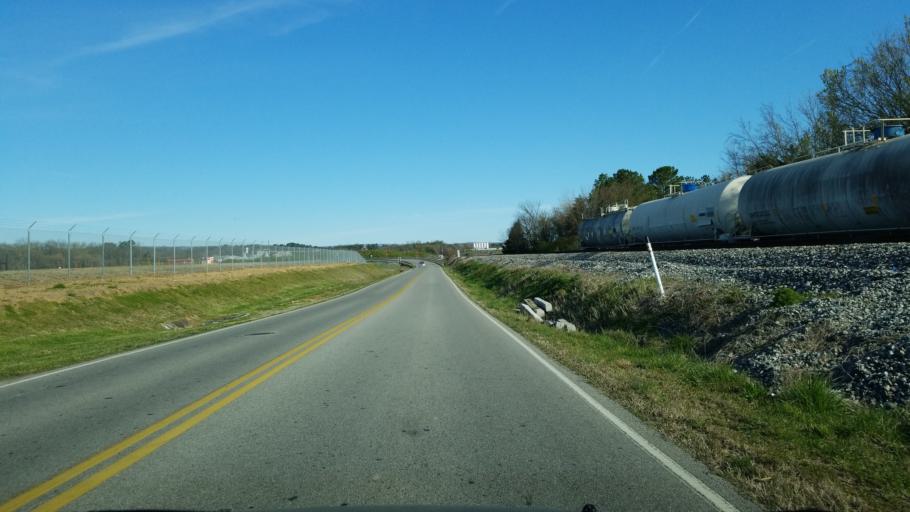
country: US
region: Tennessee
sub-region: Hamilton County
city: East Chattanooga
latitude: 35.0425
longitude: -85.1972
